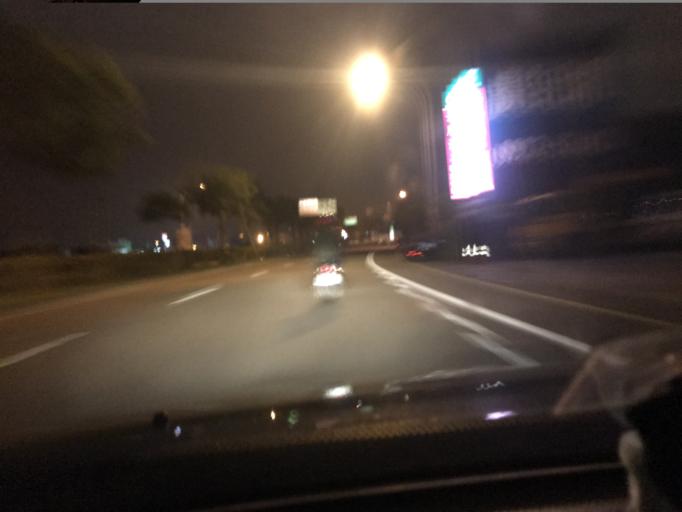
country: TW
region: Taiwan
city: Daxi
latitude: 24.8578
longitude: 121.2219
